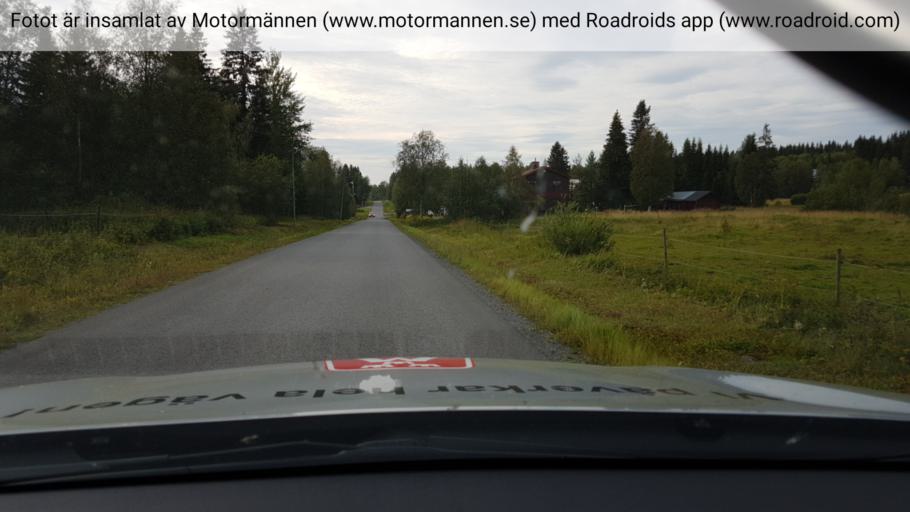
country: SE
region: Jaemtland
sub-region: OEstersunds Kommun
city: Lit
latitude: 63.5623
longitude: 14.9434
